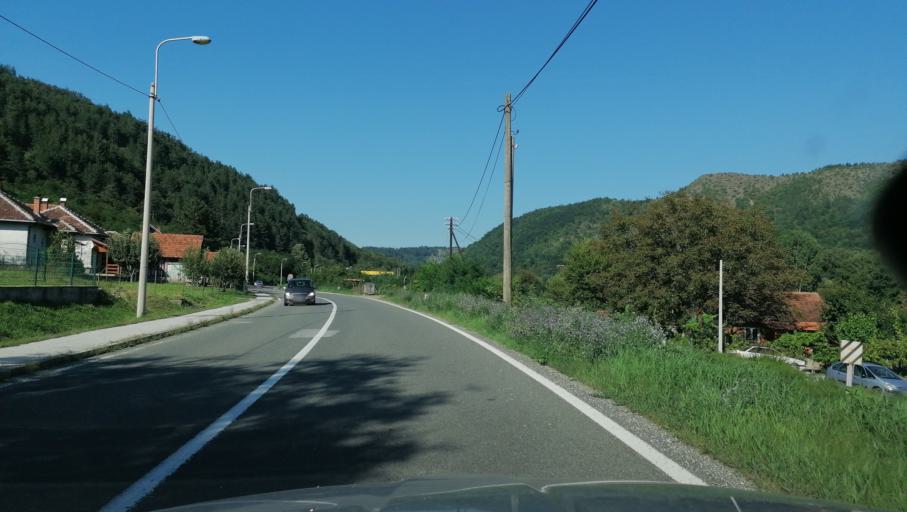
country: RS
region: Central Serbia
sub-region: Raski Okrug
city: Kraljevo
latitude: 43.6510
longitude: 20.5552
